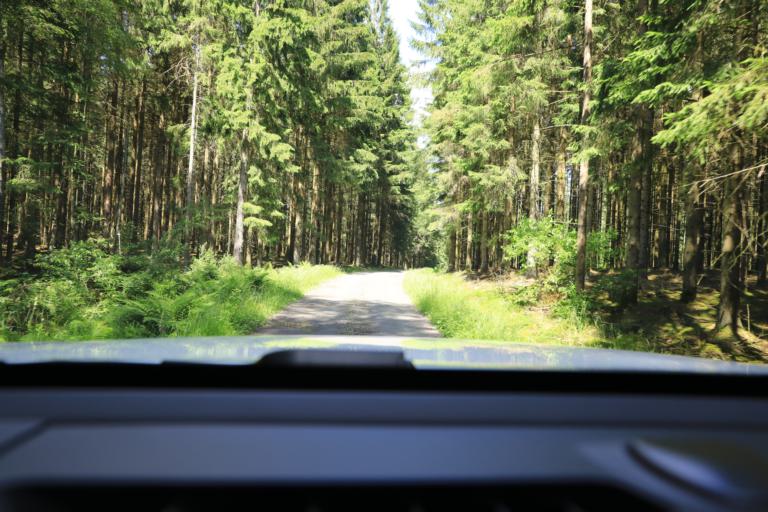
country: SE
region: Halland
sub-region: Varbergs Kommun
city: Tvaaker
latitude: 57.0981
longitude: 12.4823
